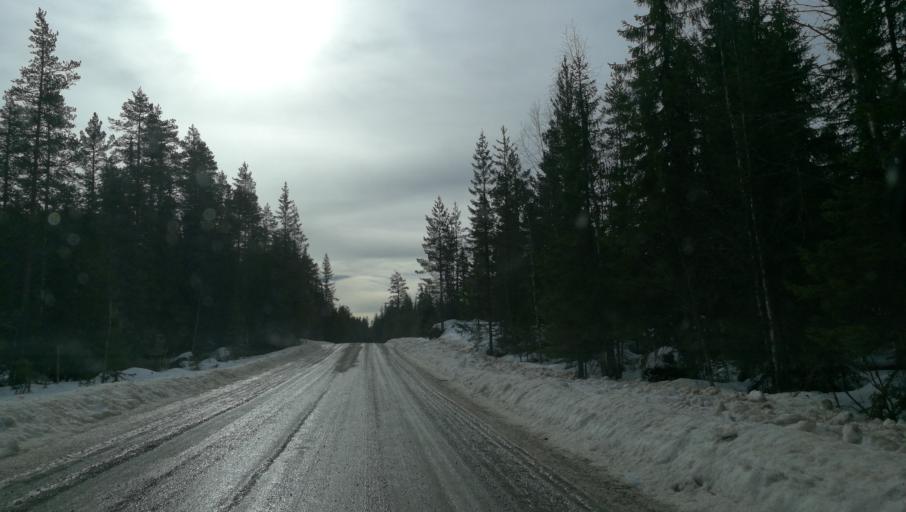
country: SE
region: Vaermland
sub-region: Torsby Kommun
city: Torsby
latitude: 60.6723
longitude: 12.8747
